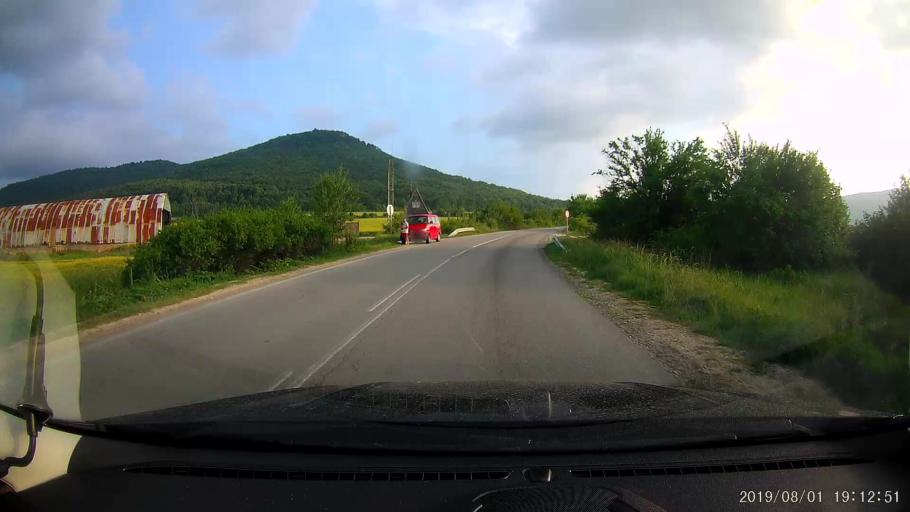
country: BG
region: Shumen
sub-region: Obshtina Smyadovo
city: Smyadovo
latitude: 42.9589
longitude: 26.9474
